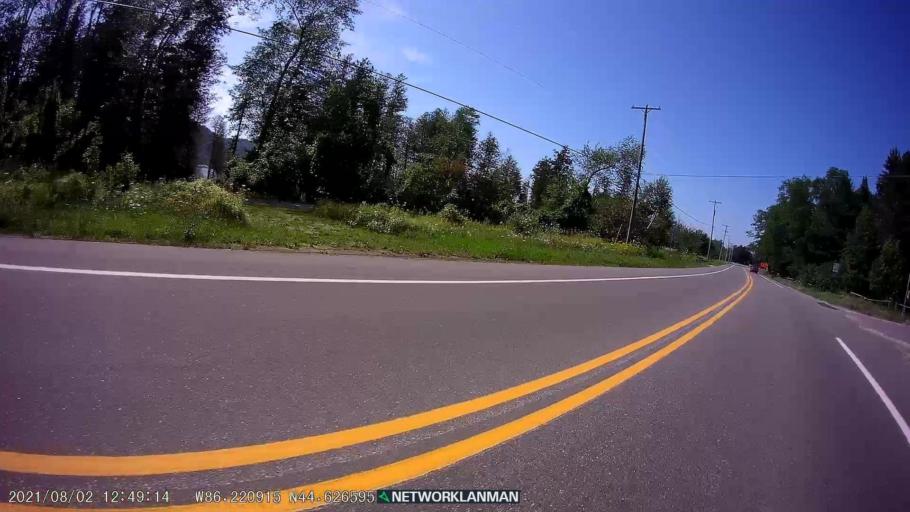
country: US
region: Michigan
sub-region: Benzie County
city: Frankfort
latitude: 44.6268
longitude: -86.2210
